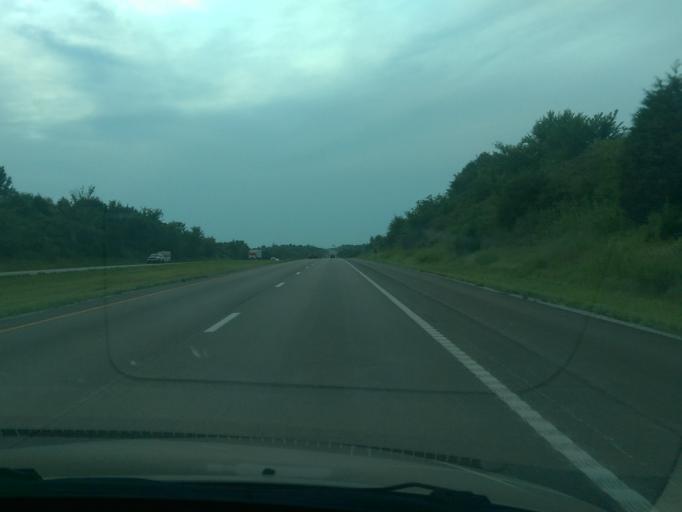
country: US
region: Missouri
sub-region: Andrew County
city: Country Club Village
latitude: 39.8780
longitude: -94.8427
